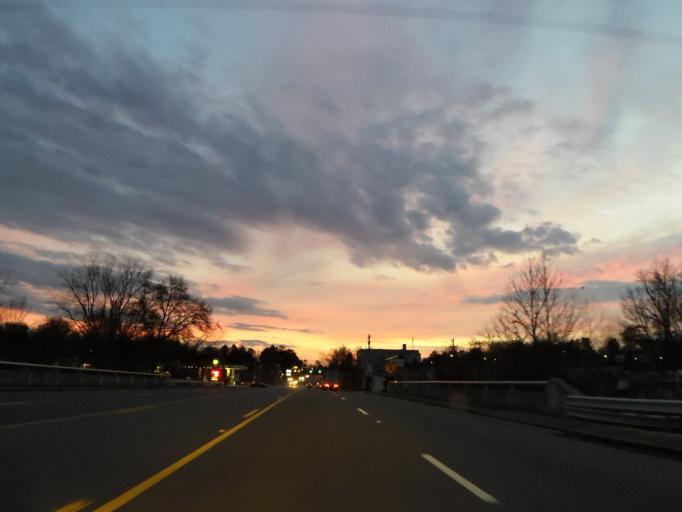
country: US
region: Tennessee
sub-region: Polk County
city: Benton
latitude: 35.1749
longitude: -84.6517
